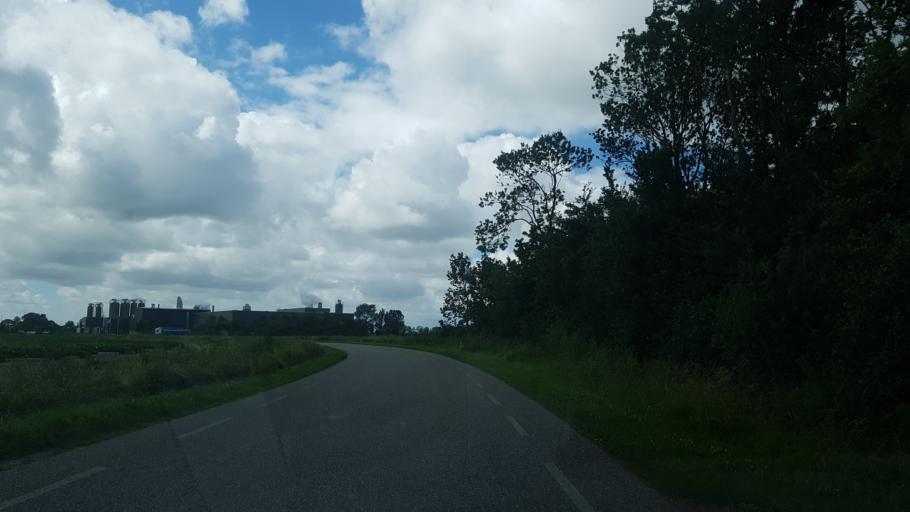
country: NL
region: Groningen
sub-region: Gemeente Winsum
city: Winsum
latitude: 53.3938
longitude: 6.5329
